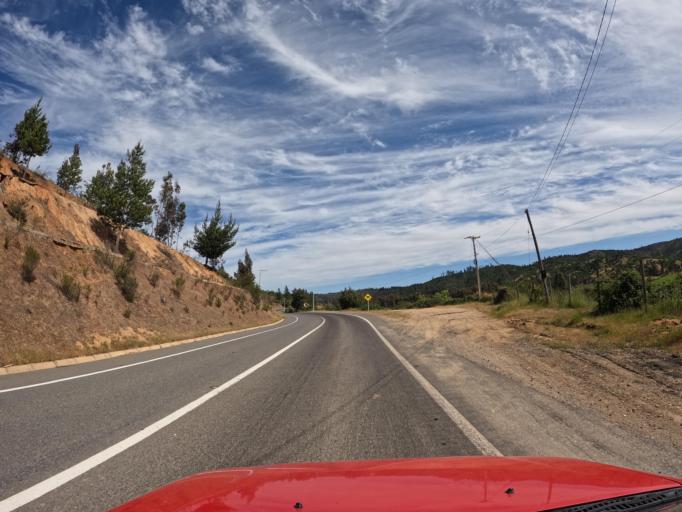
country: CL
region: Maule
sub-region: Provincia de Talca
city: Talca
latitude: -35.1375
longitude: -71.9633
